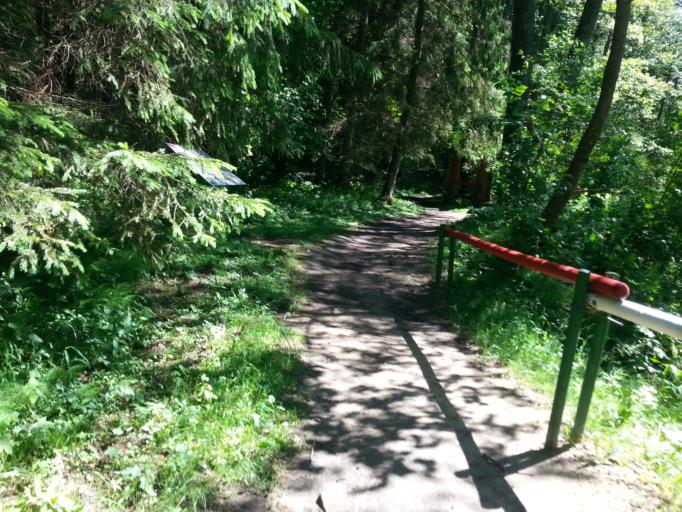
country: BY
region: Vitebsk
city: Lyntupy
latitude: 54.9622
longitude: 26.3661
